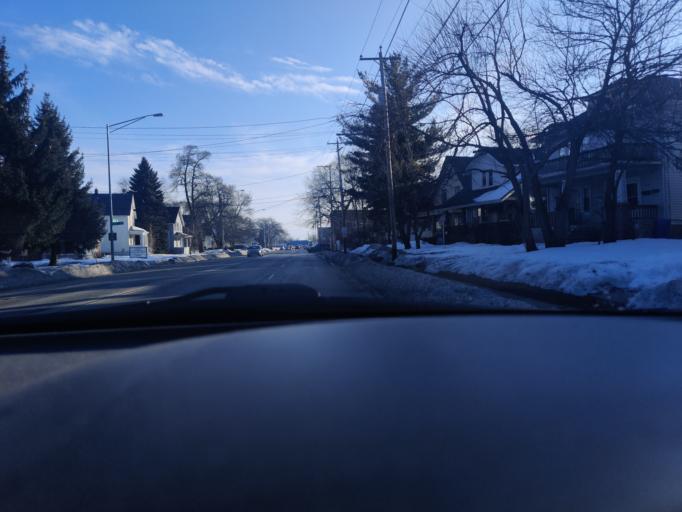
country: US
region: Wisconsin
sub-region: Kenosha County
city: Kenosha
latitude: 42.5723
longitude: -87.8231
